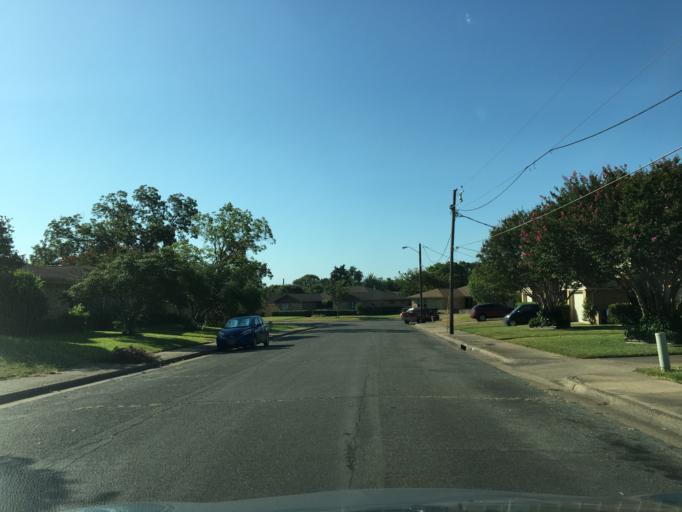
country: US
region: Texas
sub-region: Dallas County
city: Garland
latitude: 32.8611
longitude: -96.7034
